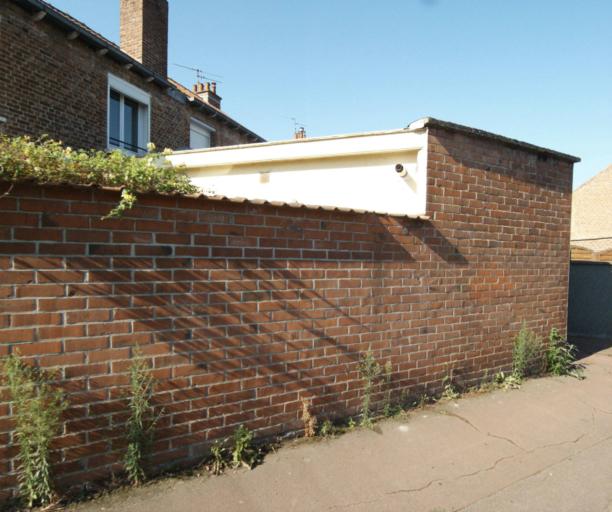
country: FR
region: Nord-Pas-de-Calais
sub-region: Departement du Nord
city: Mons-en-Baroeul
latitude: 50.6284
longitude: 3.1174
